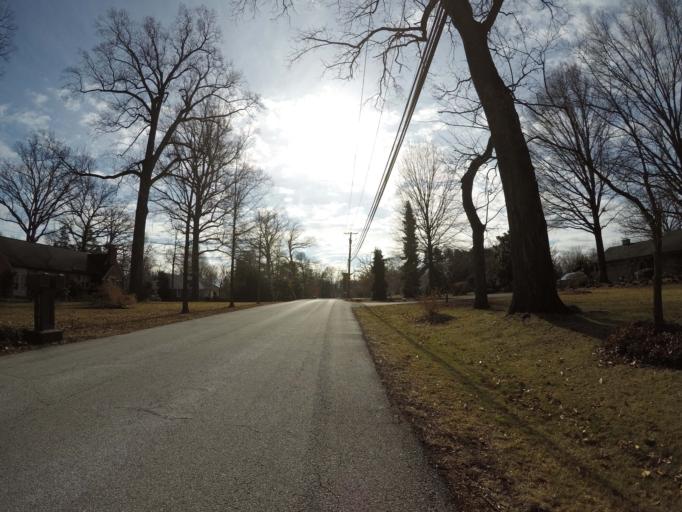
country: US
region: Maryland
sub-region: Howard County
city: Columbia
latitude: 39.2693
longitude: -76.8329
